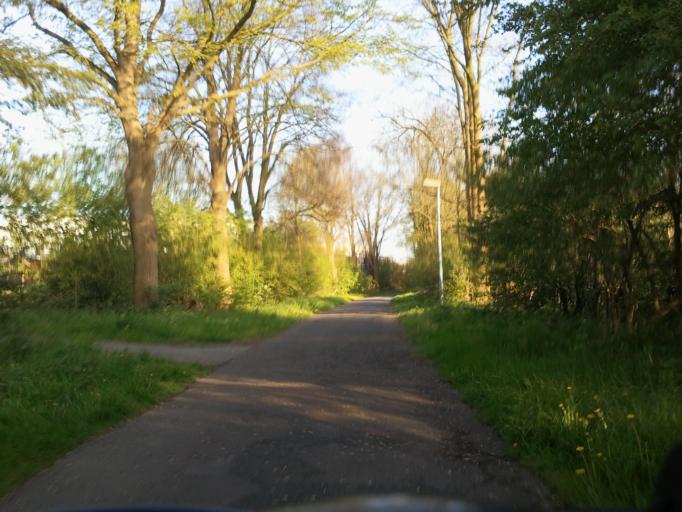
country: DE
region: Lower Saxony
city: Nienburg
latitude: 52.6427
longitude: 9.1979
